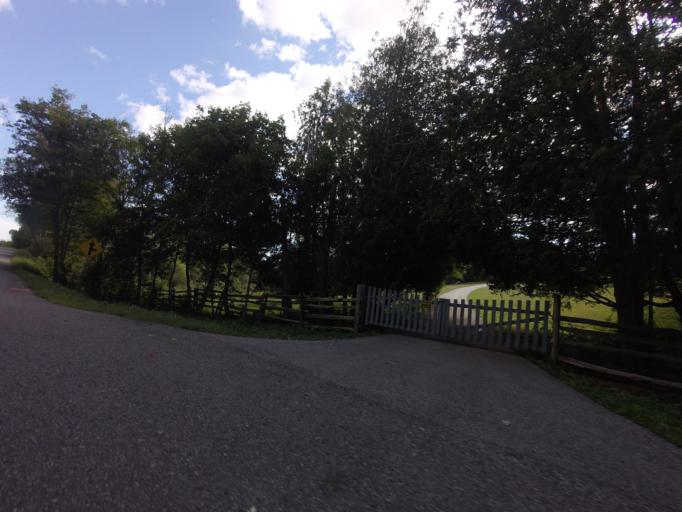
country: CA
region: Ontario
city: Orangeville
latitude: 43.8221
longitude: -79.9927
